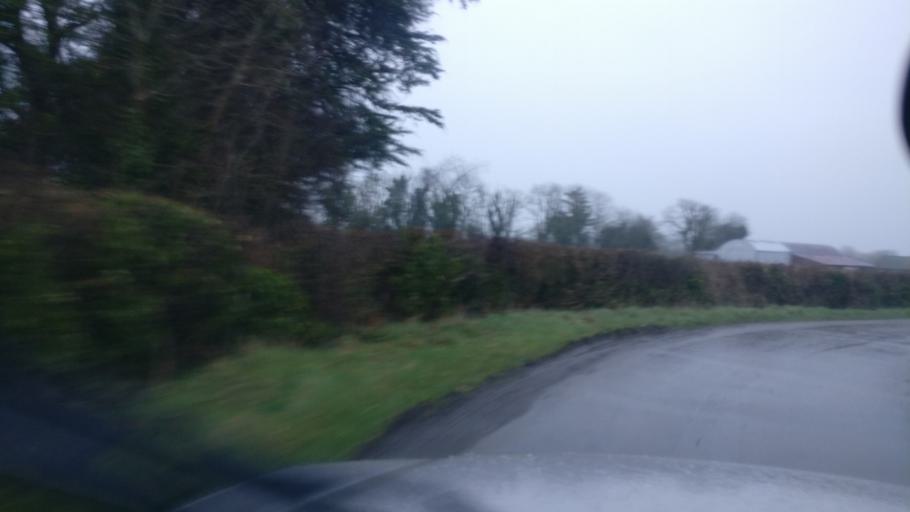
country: IE
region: Connaught
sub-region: County Galway
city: Ballinasloe
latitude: 53.3112
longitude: -8.3582
